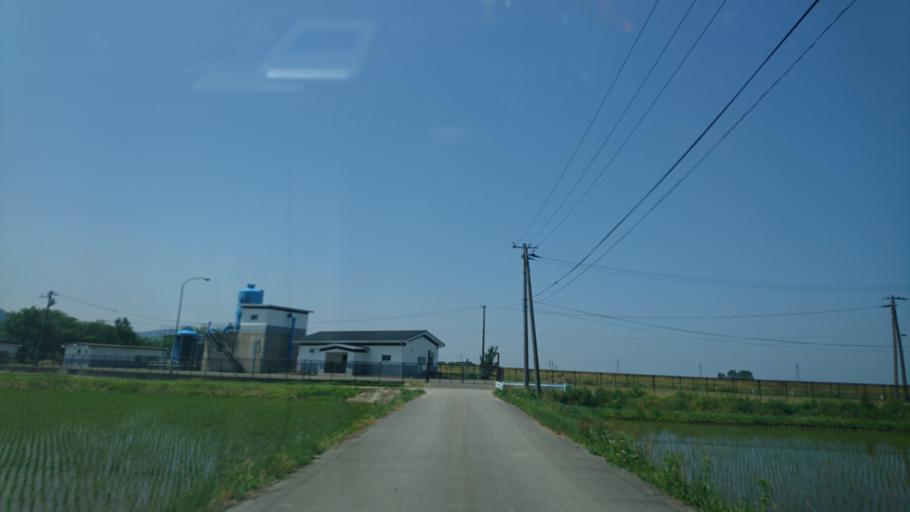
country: JP
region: Niigata
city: Murakami
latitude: 38.1246
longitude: 139.4758
